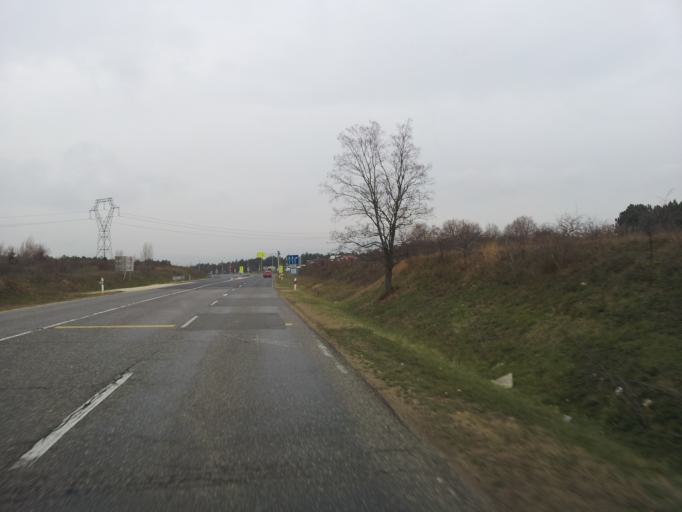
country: HU
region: Veszprem
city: Veszprem
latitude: 47.1043
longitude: 17.8681
